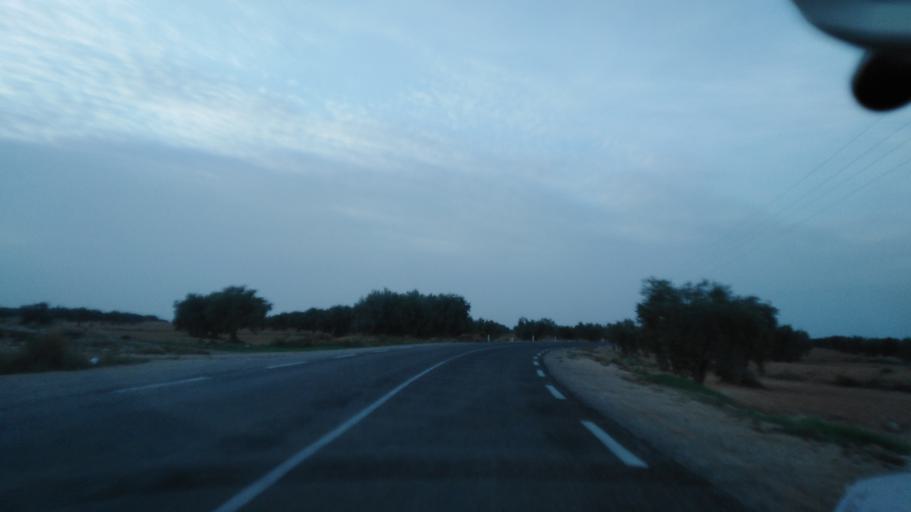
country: TN
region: Safaqis
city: Bi'r `Ali Bin Khalifah
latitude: 34.9026
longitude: 10.3882
